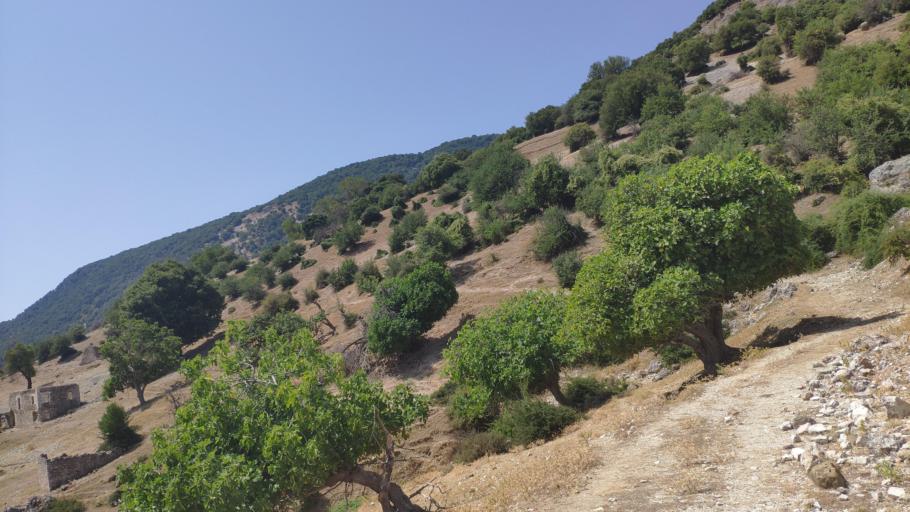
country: GR
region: West Greece
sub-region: Nomos Aitolias kai Akarnanias
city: Monastirakion
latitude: 38.8143
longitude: 21.0170
